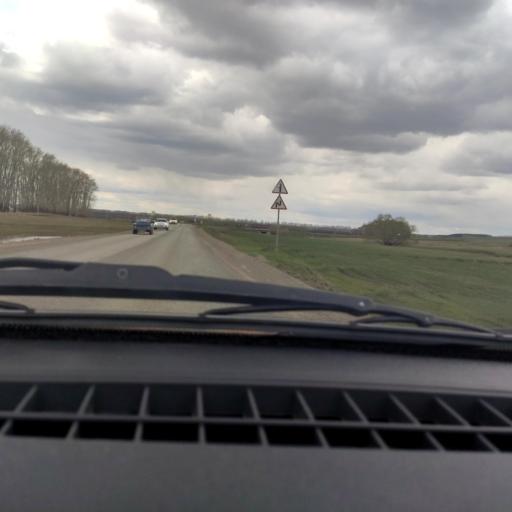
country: RU
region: Bashkortostan
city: Chekmagush
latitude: 55.1163
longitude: 54.7582
